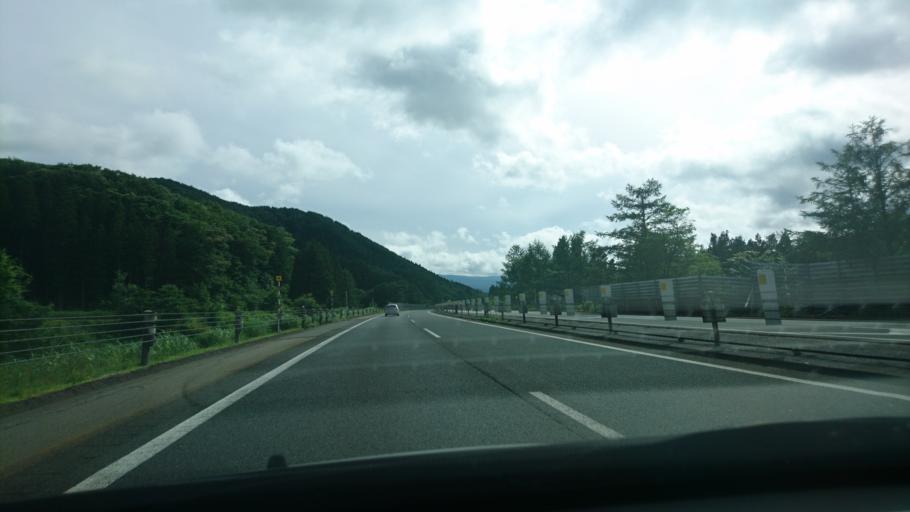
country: JP
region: Akita
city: Hanawa
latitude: 40.0523
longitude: 141.0145
